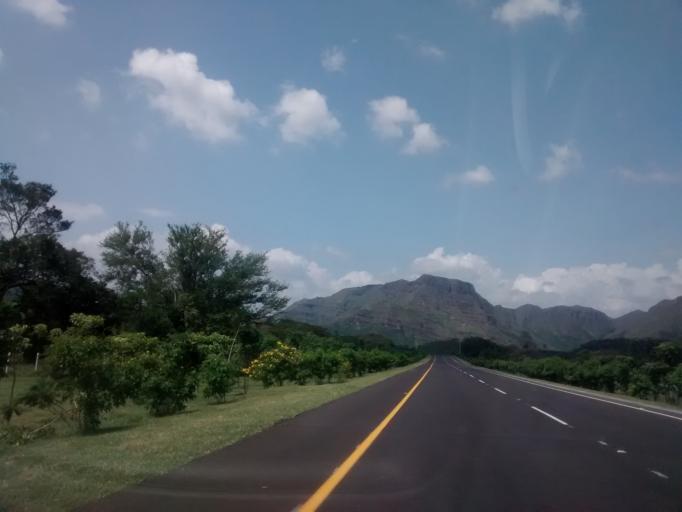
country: CO
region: Tolima
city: Valle de San Juan
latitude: 4.2730
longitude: -75.0013
